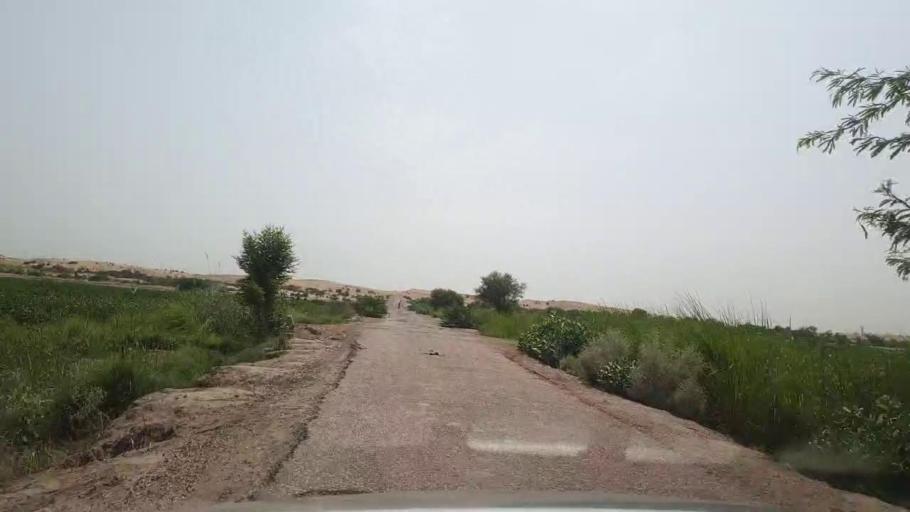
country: PK
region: Sindh
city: Rohri
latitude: 27.6180
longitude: 69.1115
